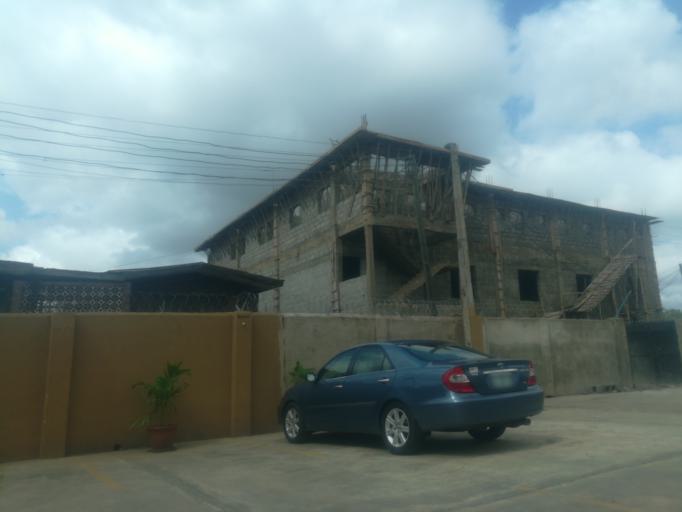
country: NG
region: Oyo
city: Ibadan
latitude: 7.3641
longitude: 3.8748
